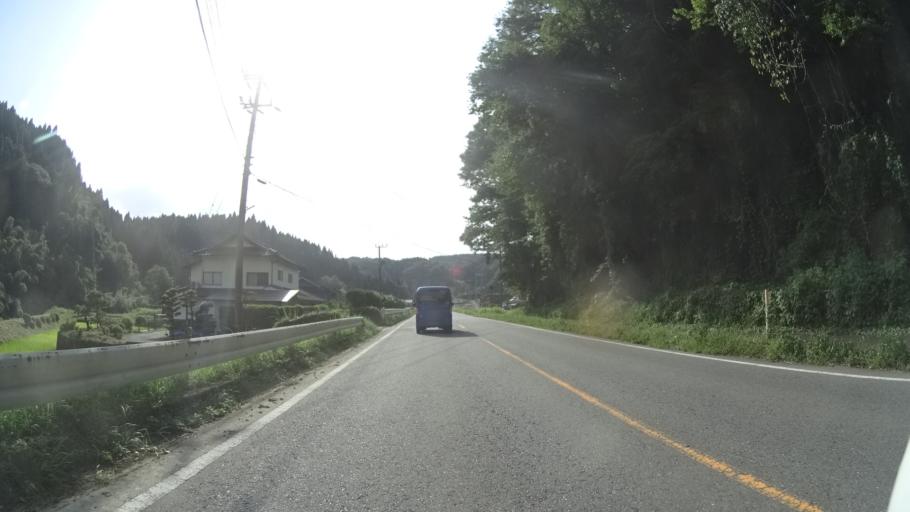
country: JP
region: Kumamoto
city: Aso
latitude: 32.6854
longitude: 131.0491
